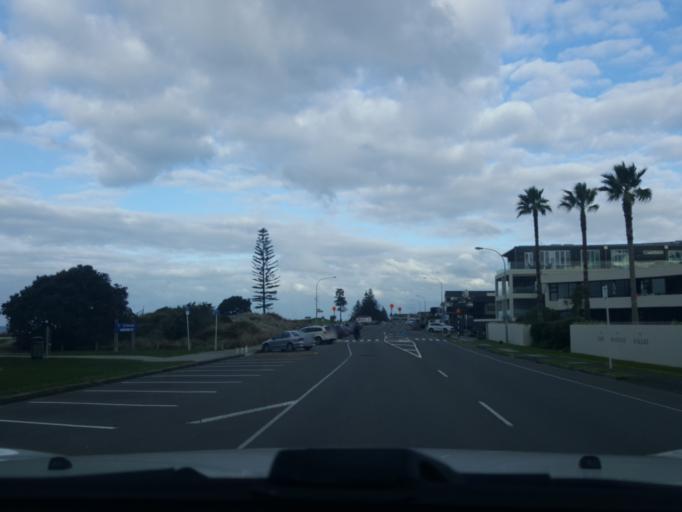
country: NZ
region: Bay of Plenty
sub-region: Tauranga City
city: Tauranga
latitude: -37.6463
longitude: 176.1979
